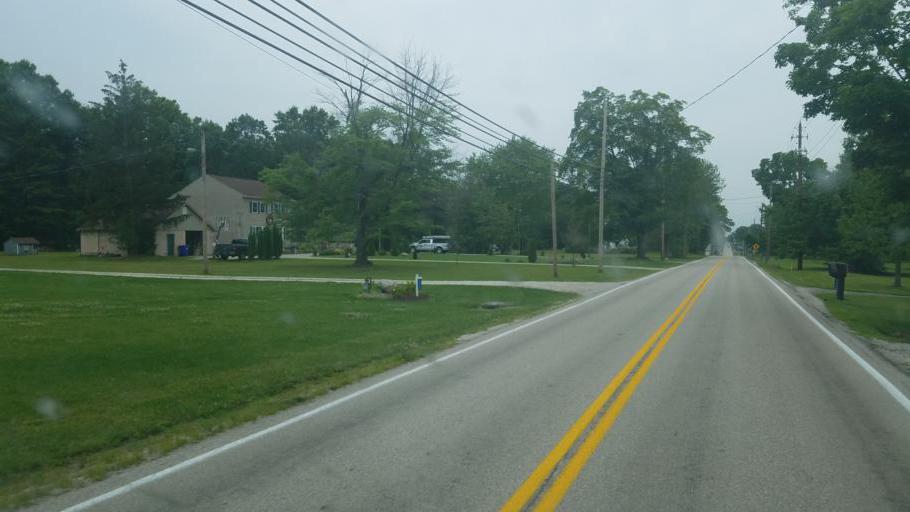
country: US
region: Ohio
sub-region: Portage County
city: Ravenna
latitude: 41.0990
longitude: -81.2286
